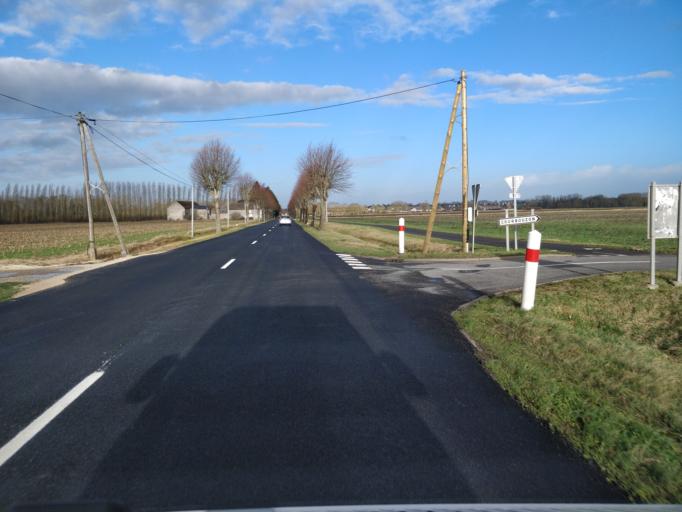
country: FR
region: Centre
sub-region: Departement du Loir-et-Cher
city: Muides-sur-Loire
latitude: 47.6820
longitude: 1.5208
